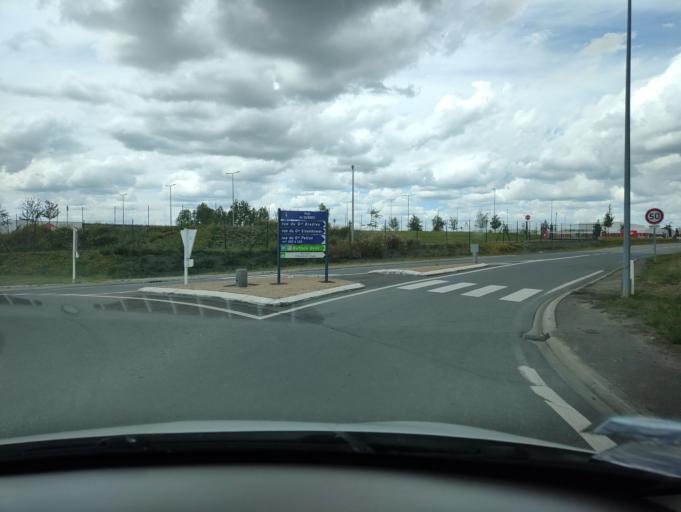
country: FR
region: Pays de la Loire
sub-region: Departement de la Loire-Atlantique
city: Chateaubriant
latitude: 47.7043
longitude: -1.3933
